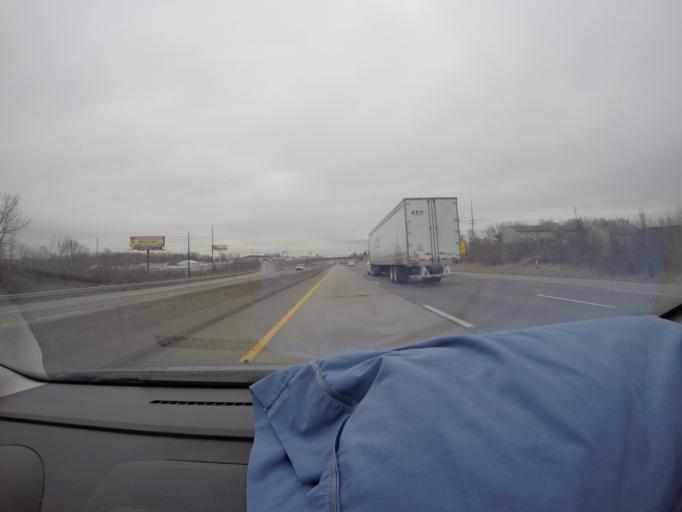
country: US
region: Missouri
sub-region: Saint Charles County
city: Dardenne Prairie
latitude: 38.8032
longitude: -90.7370
